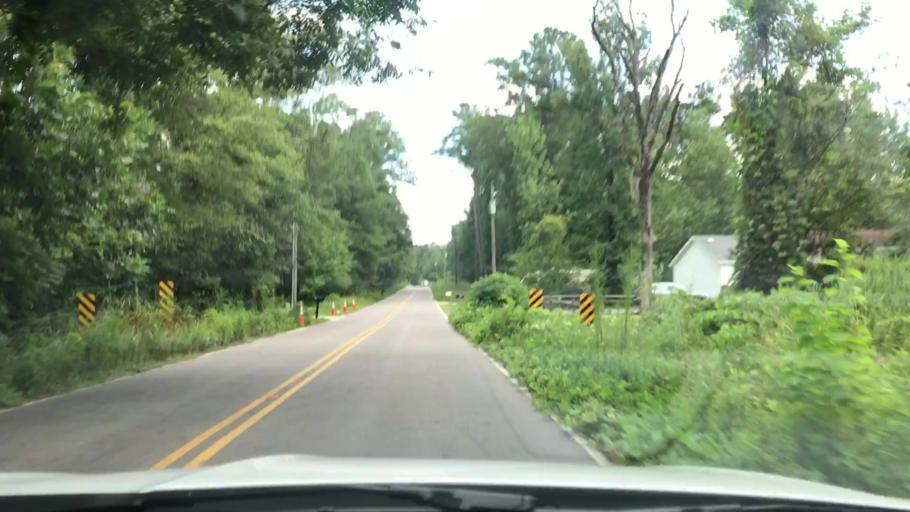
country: US
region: South Carolina
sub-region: Dorchester County
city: Summerville
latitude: 33.0349
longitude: -80.2132
